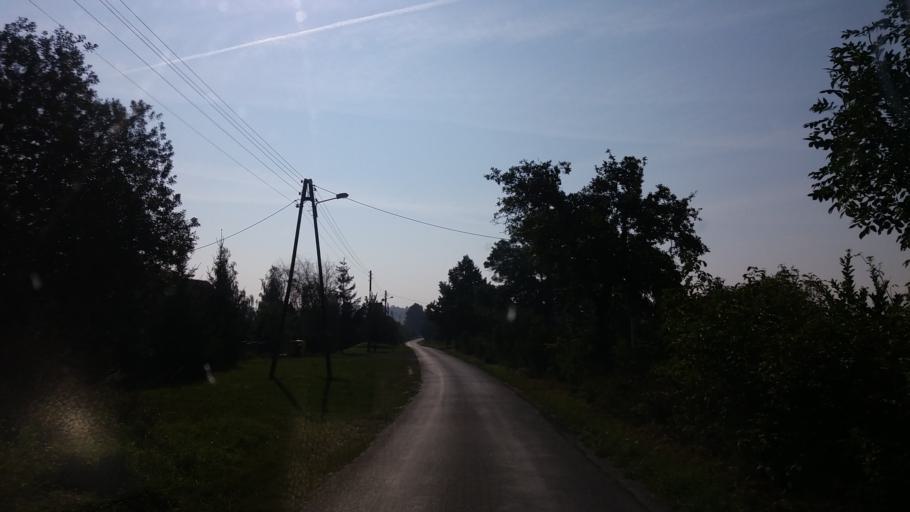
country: PL
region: West Pomeranian Voivodeship
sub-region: Powiat choszczenski
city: Pelczyce
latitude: 53.0210
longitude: 15.3296
